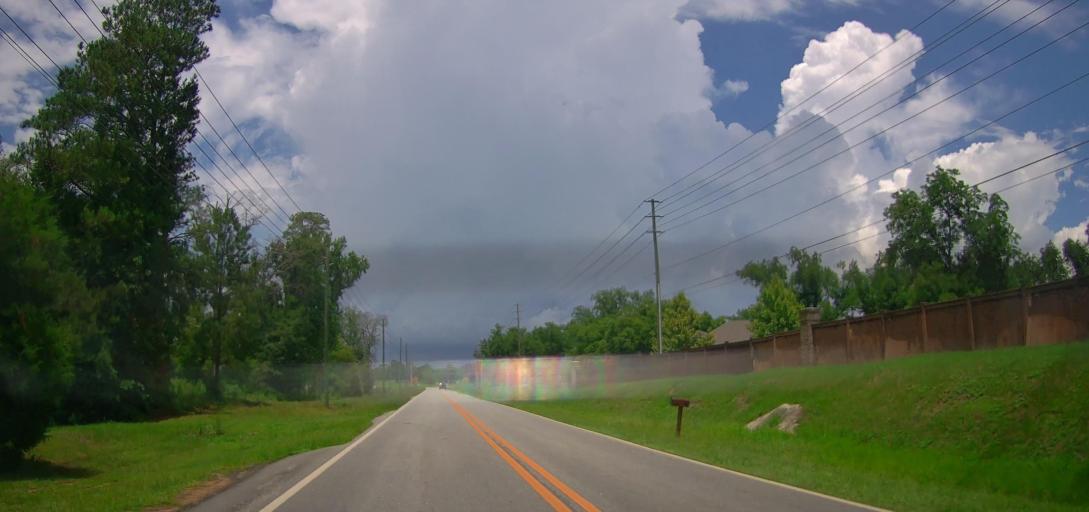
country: US
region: Georgia
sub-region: Houston County
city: Perry
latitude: 32.4970
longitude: -83.6638
